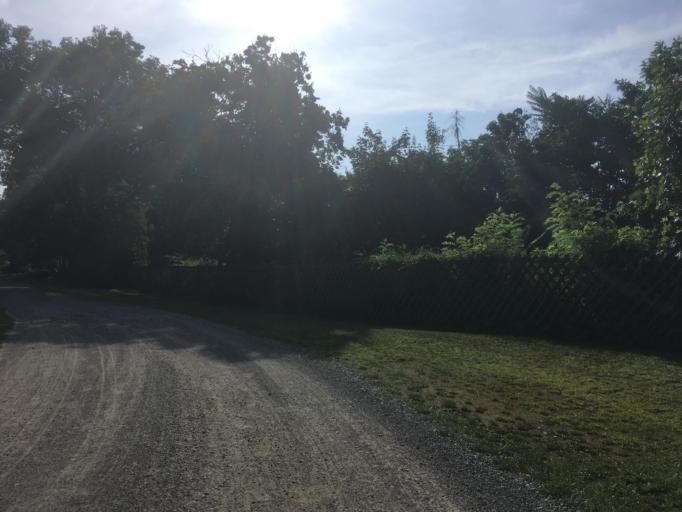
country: DE
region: Saxony-Anhalt
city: Wittenburg
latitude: 51.8658
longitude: 12.6662
